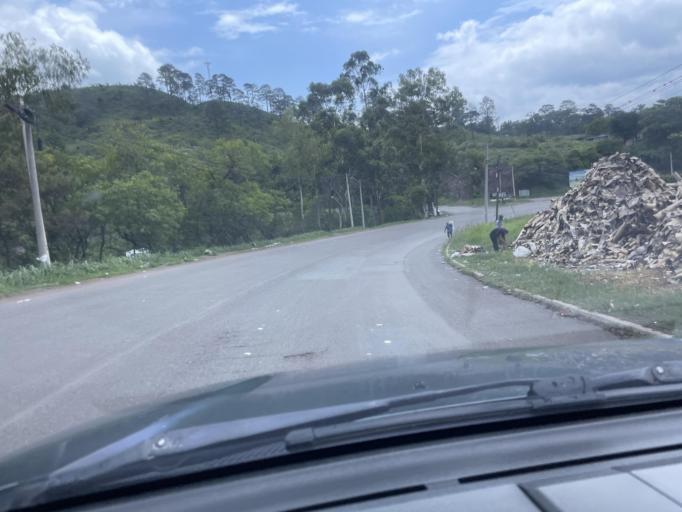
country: HN
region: Francisco Morazan
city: Rio Abajo
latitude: 14.1441
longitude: -87.2311
